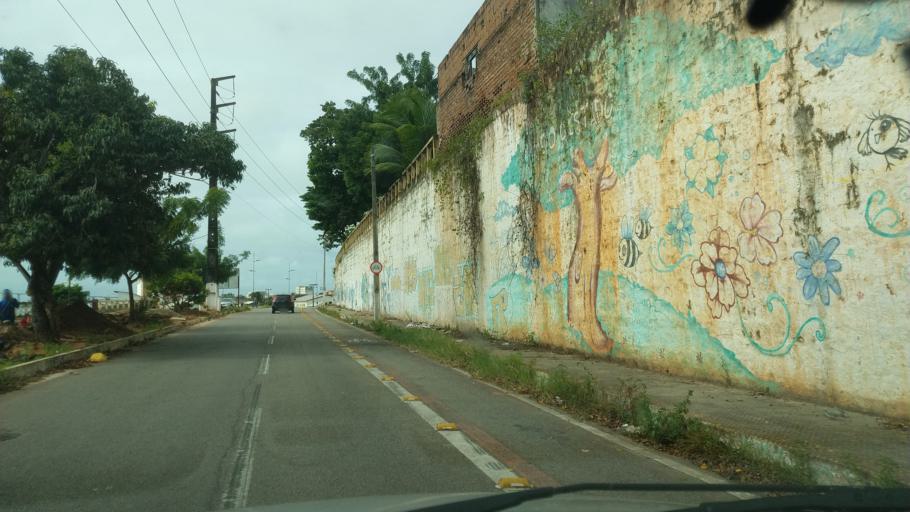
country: BR
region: Rio Grande do Norte
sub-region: Natal
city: Natal
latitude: -5.7833
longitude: -35.2100
